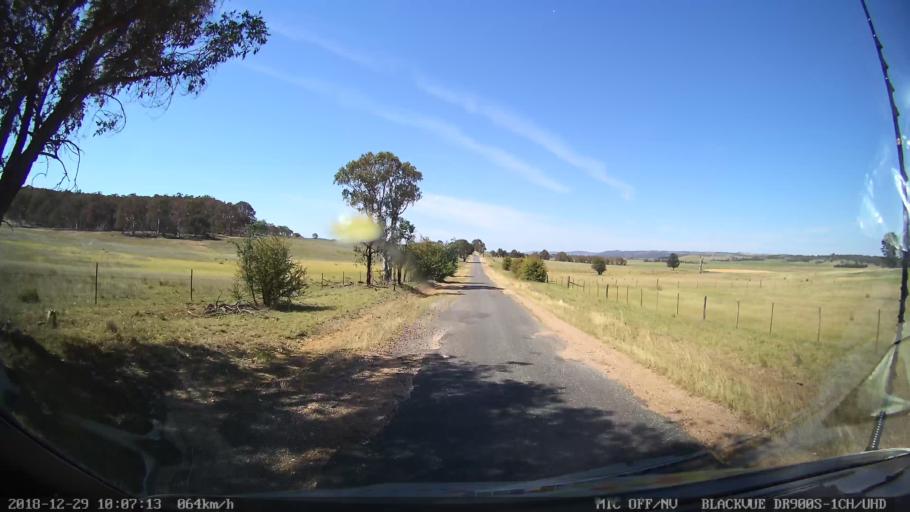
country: AU
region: New South Wales
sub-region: Yass Valley
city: Gundaroo
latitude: -34.8505
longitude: 149.4535
